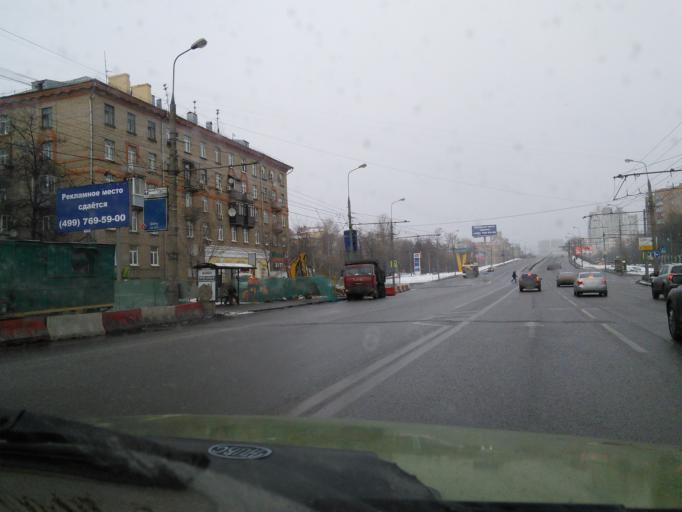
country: RU
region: Moscow
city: Sokol
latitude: 55.7945
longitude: 37.4952
